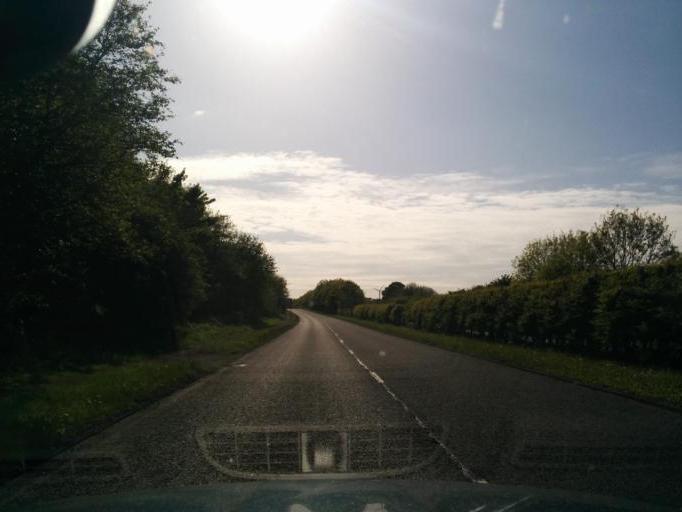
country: GB
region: England
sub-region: Northumberland
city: Cramlington
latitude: 55.1030
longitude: -1.5884
